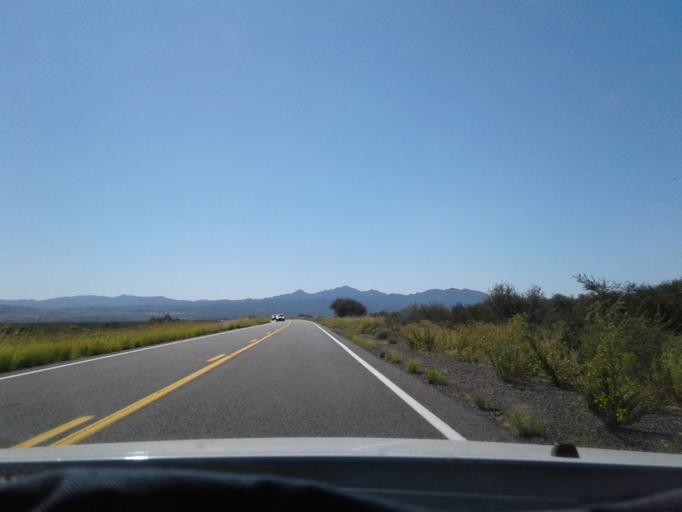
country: US
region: Arizona
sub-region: Yavapai County
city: Prescott
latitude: 34.4106
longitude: -112.6111
